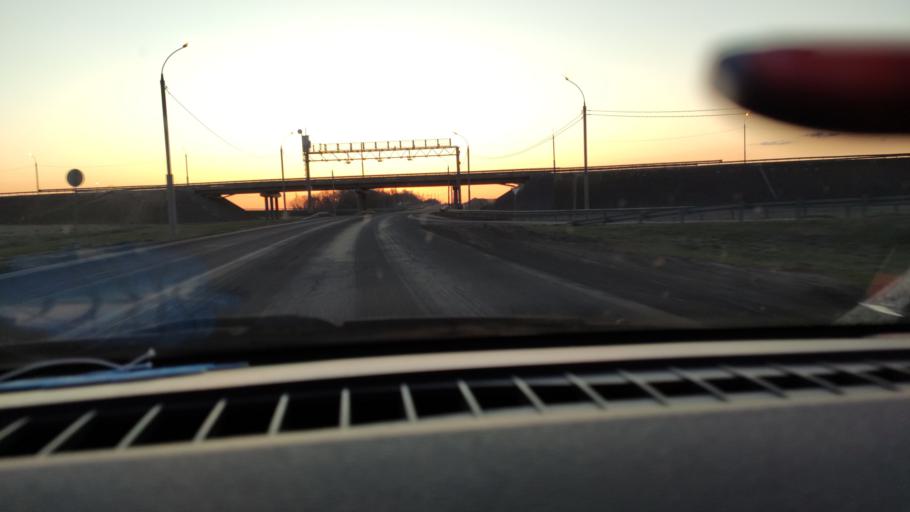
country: RU
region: Saratov
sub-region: Saratovskiy Rayon
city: Saratov
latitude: 51.7742
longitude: 46.0893
